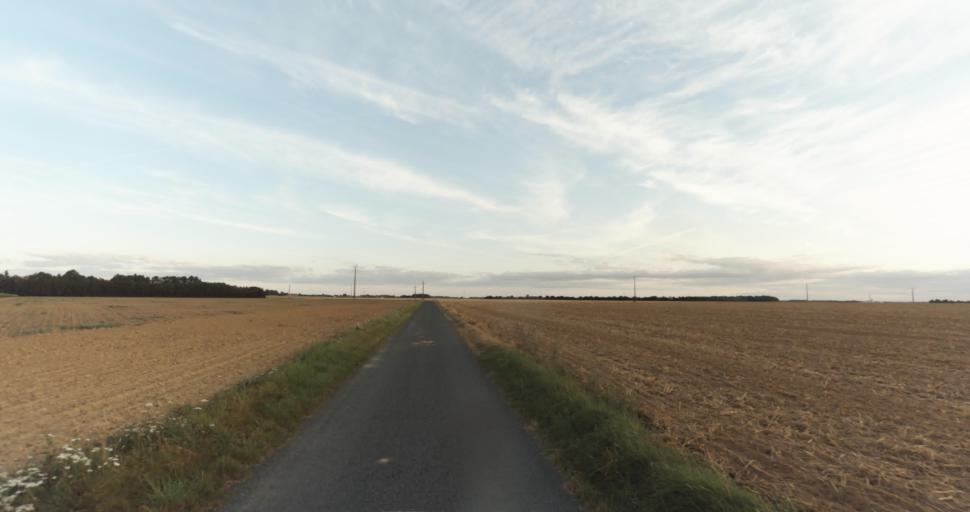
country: FR
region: Haute-Normandie
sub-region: Departement de l'Eure
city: La Madeleine-de-Nonancourt
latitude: 48.8799
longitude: 1.2281
